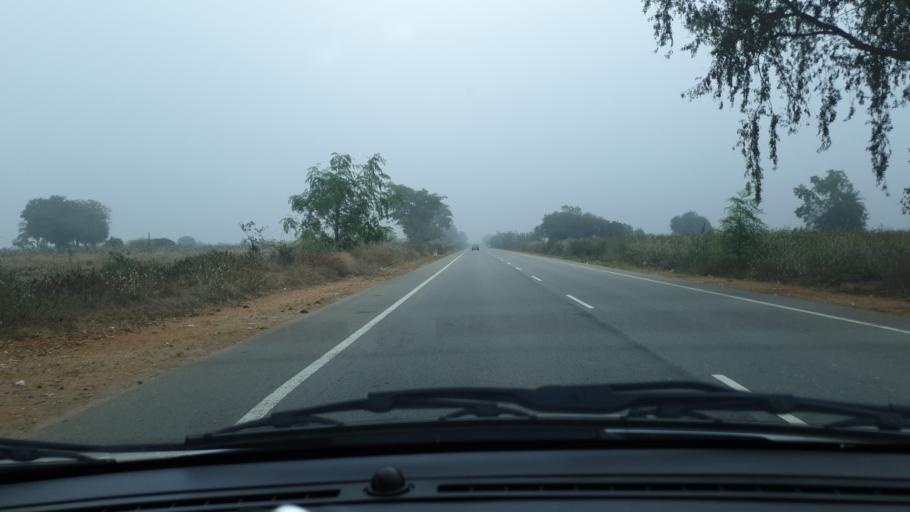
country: IN
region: Telangana
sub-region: Nalgonda
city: Devarkonda
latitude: 16.6356
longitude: 78.6373
